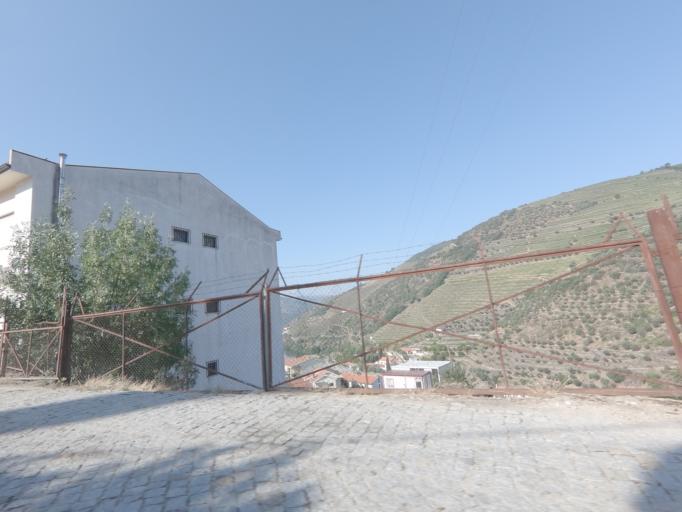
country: PT
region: Vila Real
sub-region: Sabrosa
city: Vilela
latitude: 41.1937
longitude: -7.5460
